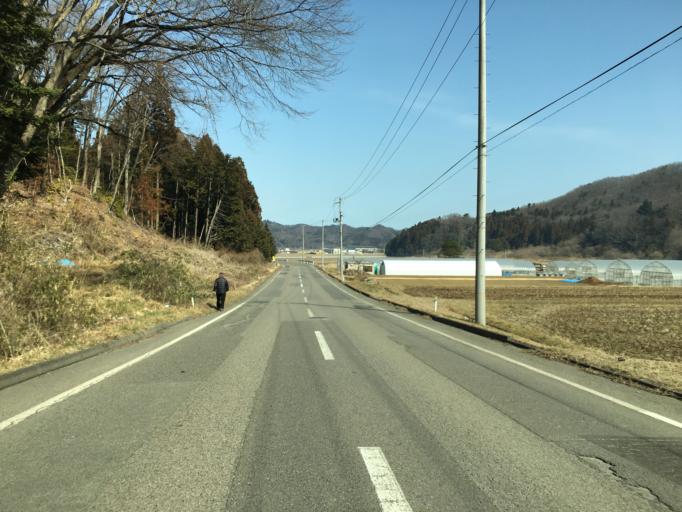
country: JP
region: Fukushima
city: Ishikawa
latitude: 37.1076
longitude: 140.2786
